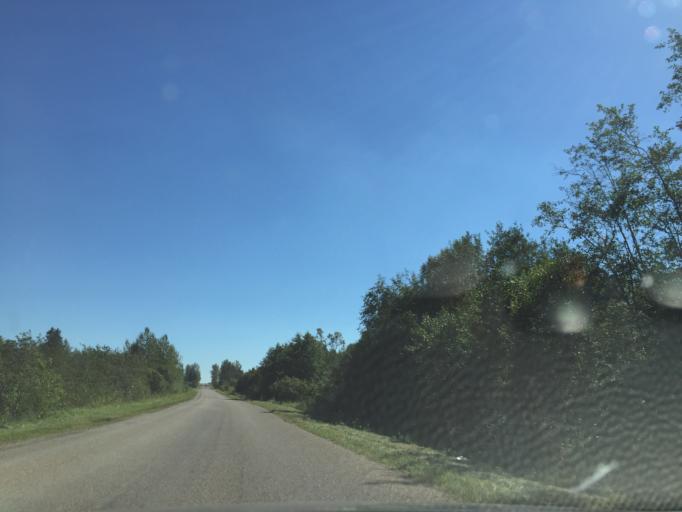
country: LV
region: Akniste
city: Akniste
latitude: 56.0368
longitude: 25.9091
